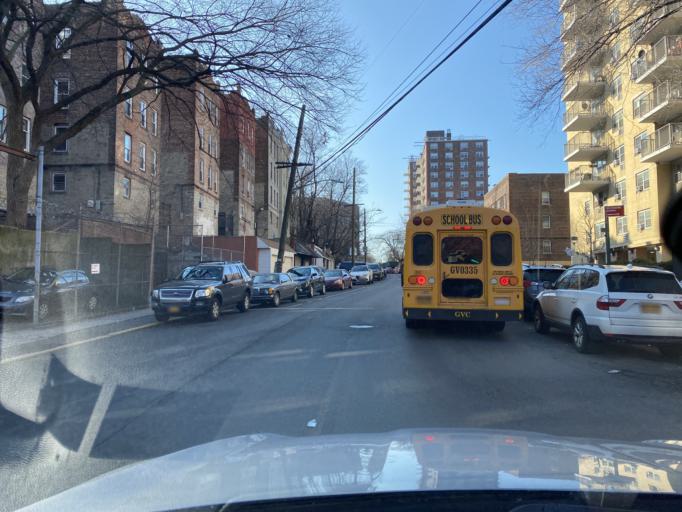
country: US
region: New York
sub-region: New York County
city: Inwood
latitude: 40.8546
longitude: -73.9170
